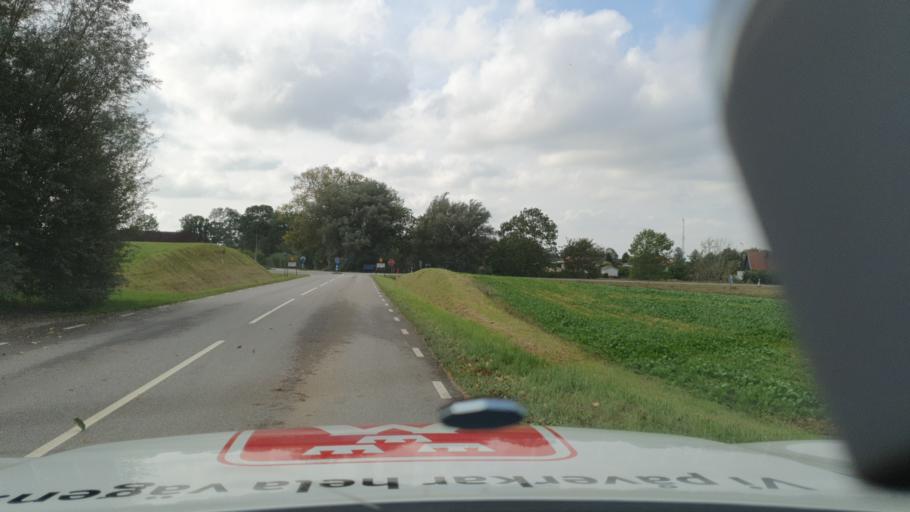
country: SE
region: Skane
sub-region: Malmo
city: Oxie
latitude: 55.4924
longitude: 13.1175
